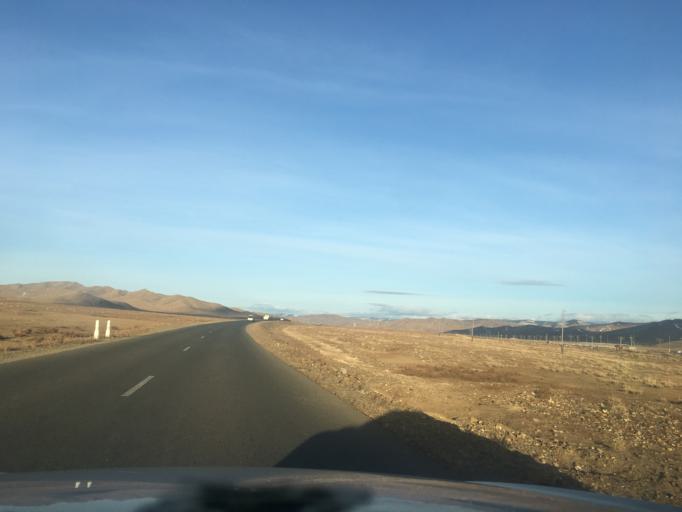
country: MN
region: Central Aimak
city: Mandal
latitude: 48.0819
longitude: 106.5863
